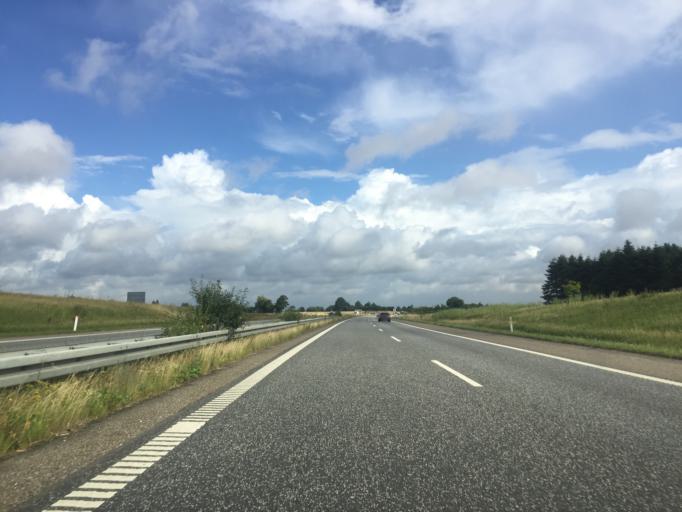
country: DK
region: South Denmark
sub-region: Faaborg-Midtfyn Kommune
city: Arslev
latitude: 55.3058
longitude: 10.4361
